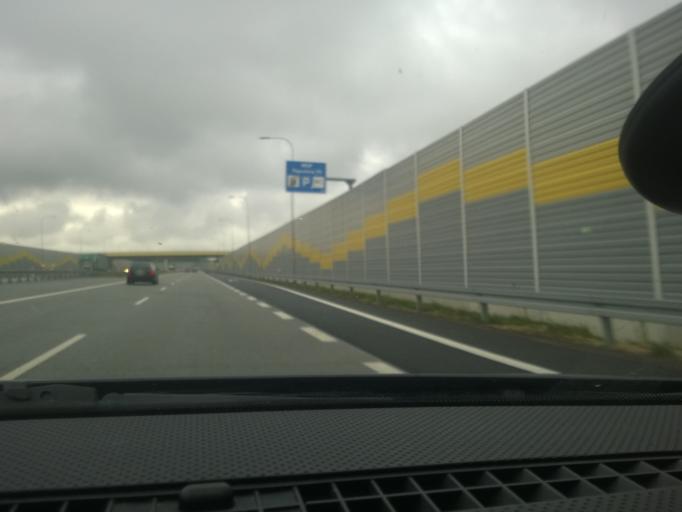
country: PL
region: Lodz Voivodeship
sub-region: Powiat zdunskowolski
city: Zdunska Wola
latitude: 51.5758
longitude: 18.9322
